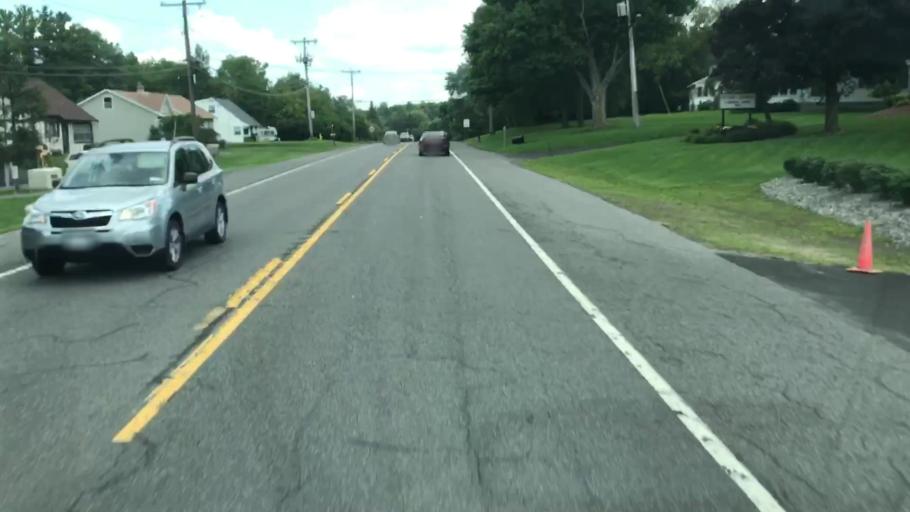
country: US
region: New York
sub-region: Onondaga County
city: Westvale
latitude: 42.9986
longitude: -76.2016
